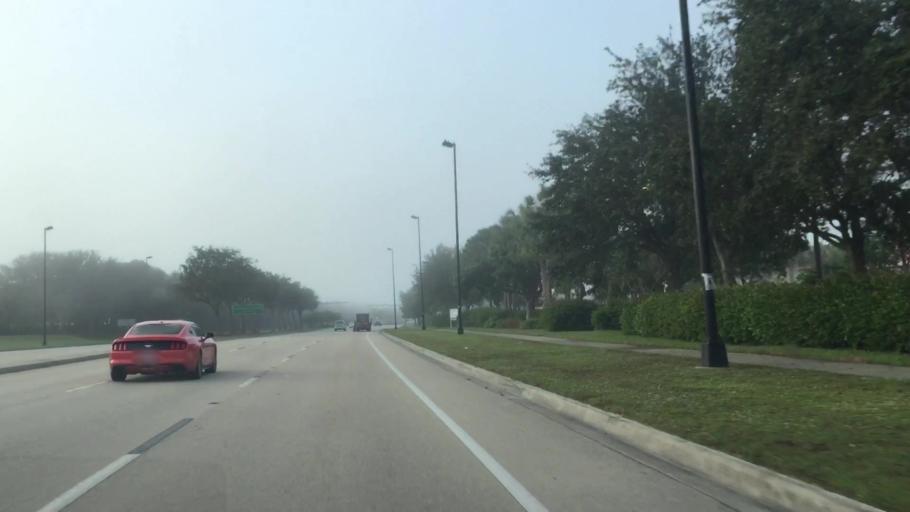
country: US
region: Florida
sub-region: Lee County
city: Three Oaks
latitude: 26.4850
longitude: -81.7844
